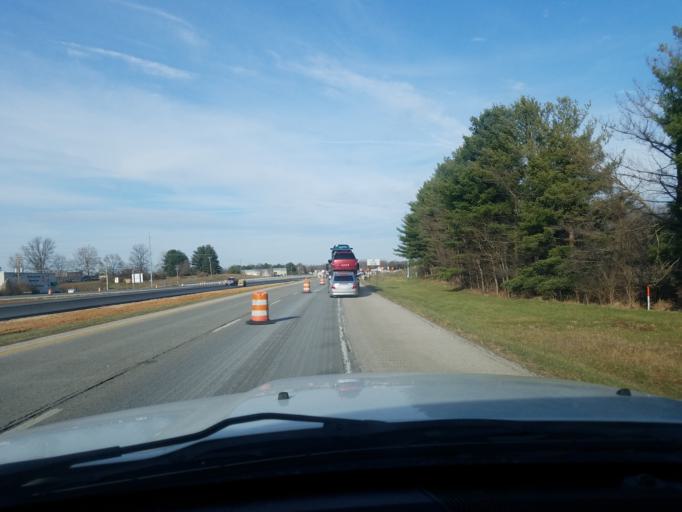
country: US
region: Indiana
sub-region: Monroe County
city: Ellettsville
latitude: 39.2785
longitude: -86.5229
